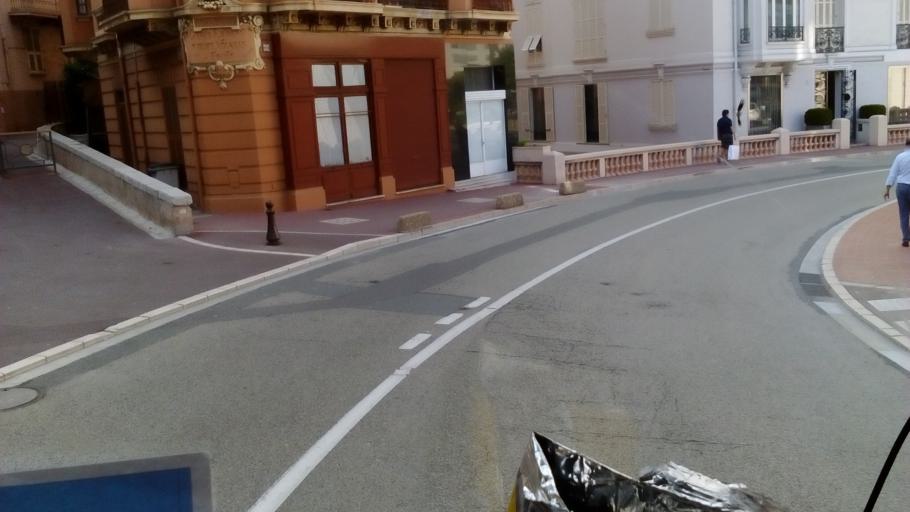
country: MC
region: Commune de Monaco
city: Saint-Roman
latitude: 43.7474
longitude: 7.4317
